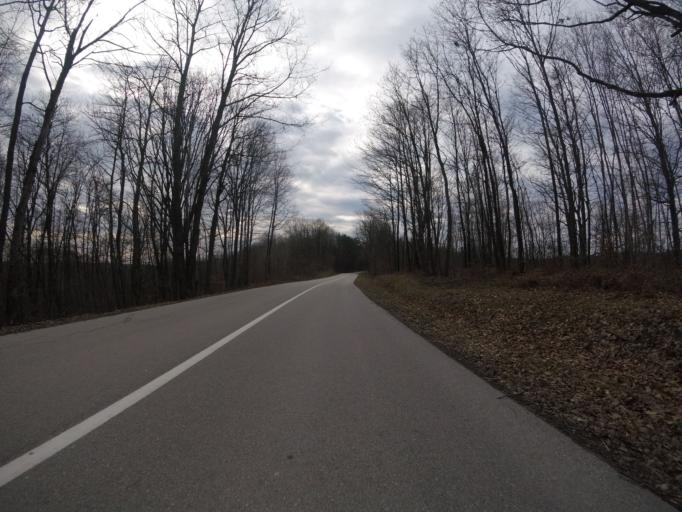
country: HR
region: Zagrebacka
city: Mraclin
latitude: 45.5375
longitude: 16.0585
